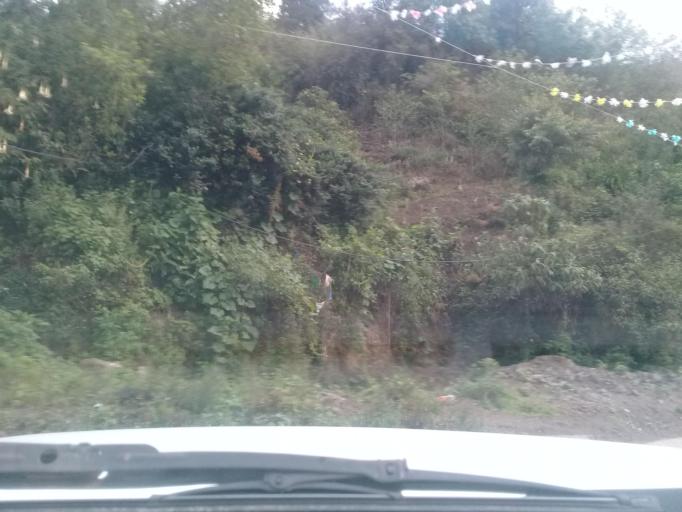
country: MX
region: Veracruz
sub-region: Mariano Escobedo
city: San Isidro el Berro
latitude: 18.9562
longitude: -97.1968
